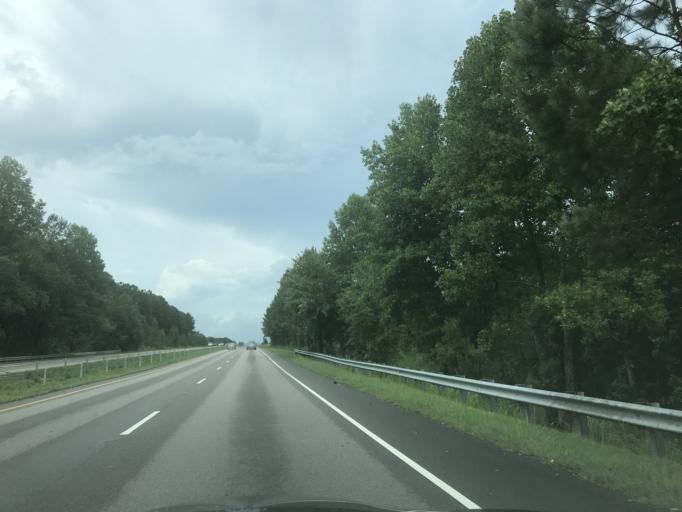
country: US
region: North Carolina
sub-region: Johnston County
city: Clayton
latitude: 35.6795
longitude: -78.5285
